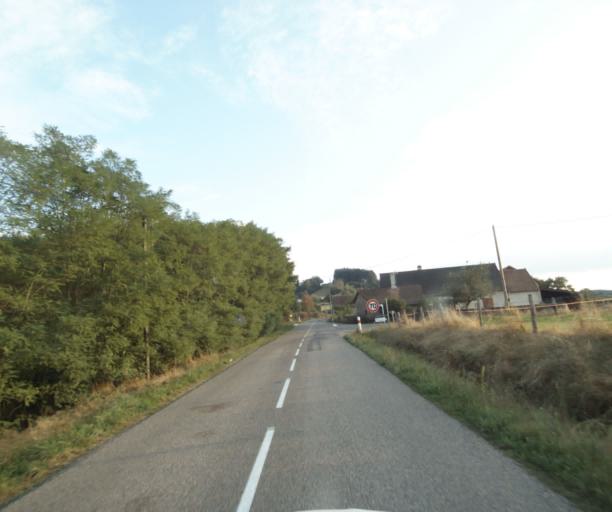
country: FR
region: Bourgogne
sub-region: Departement de Saone-et-Loire
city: Charolles
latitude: 46.4117
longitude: 4.4028
